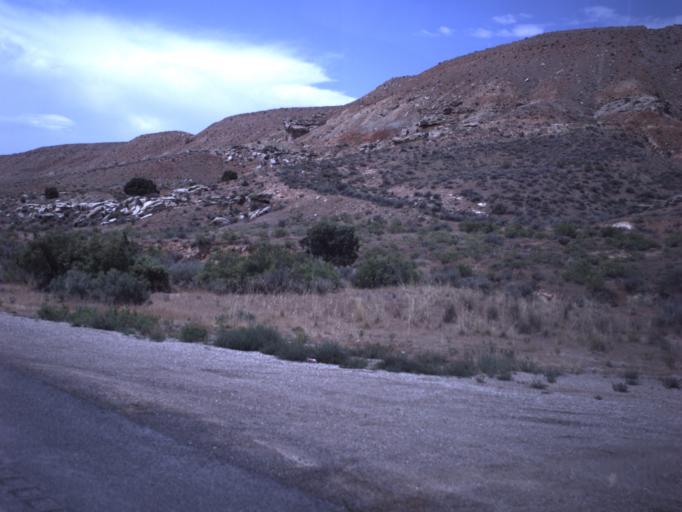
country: US
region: Utah
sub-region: Uintah County
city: Maeser
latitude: 40.3720
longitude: -109.6103
